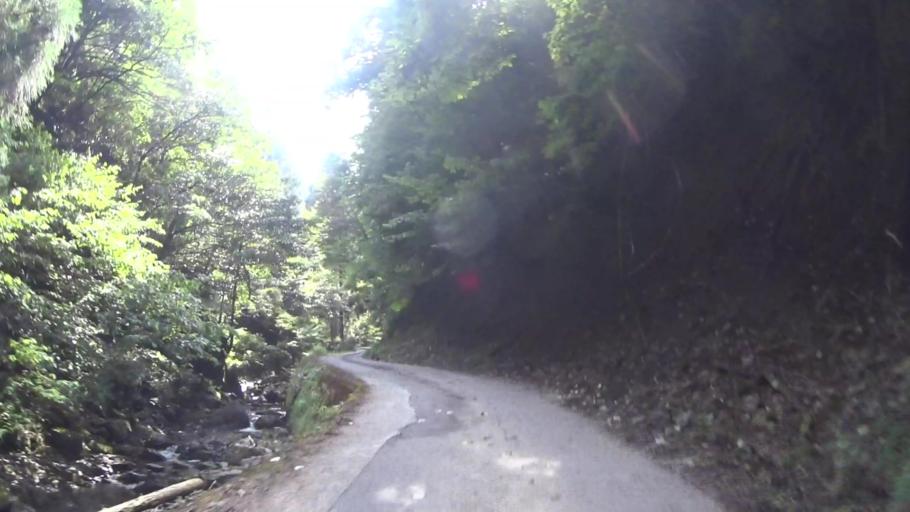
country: JP
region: Fukui
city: Obama
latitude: 35.2661
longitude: 135.6429
